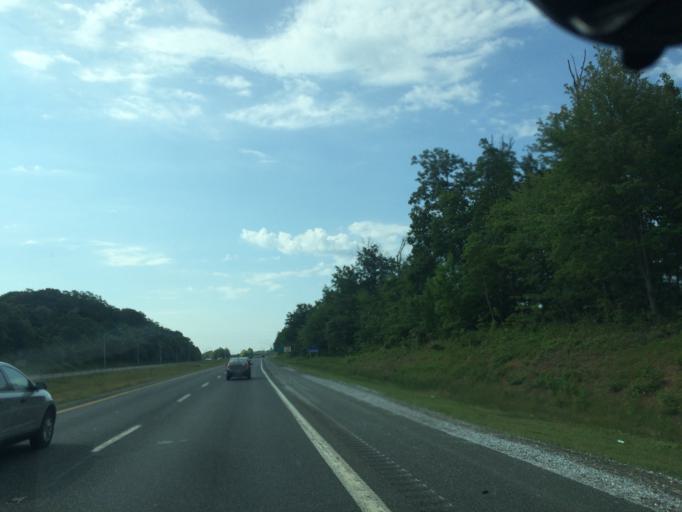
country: US
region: Maryland
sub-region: Baltimore County
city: Owings Mills
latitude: 39.4217
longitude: -76.8018
